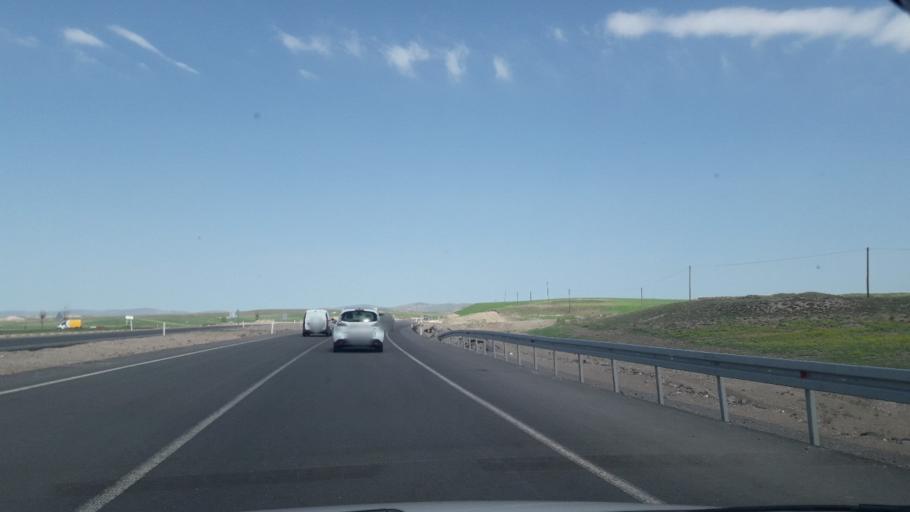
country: TR
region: Sivas
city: Deliktas
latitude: 39.2087
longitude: 37.2041
